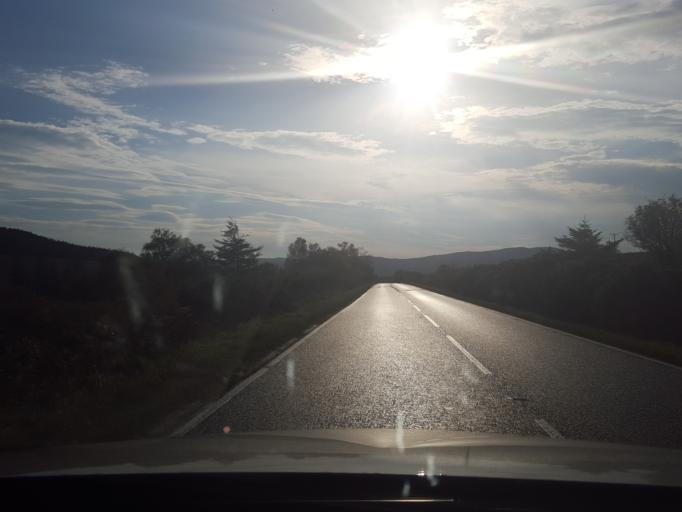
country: GB
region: Scotland
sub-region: Highland
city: Portree
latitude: 57.2564
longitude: -5.9399
